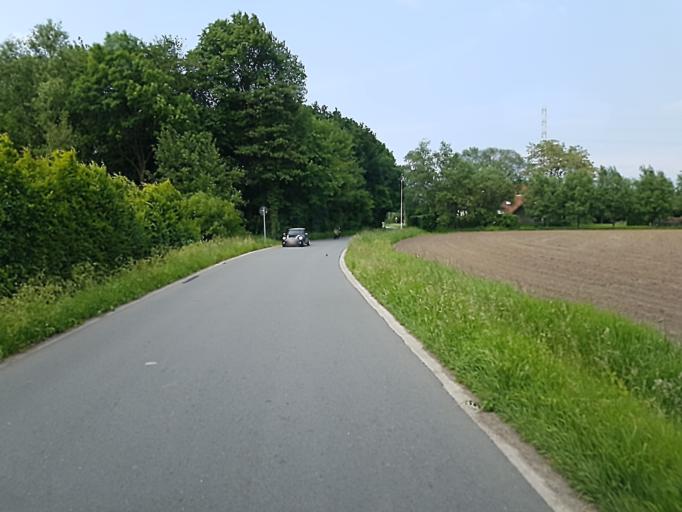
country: BE
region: Flanders
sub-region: Provincie Antwerpen
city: Ranst
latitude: 51.2133
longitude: 4.5506
